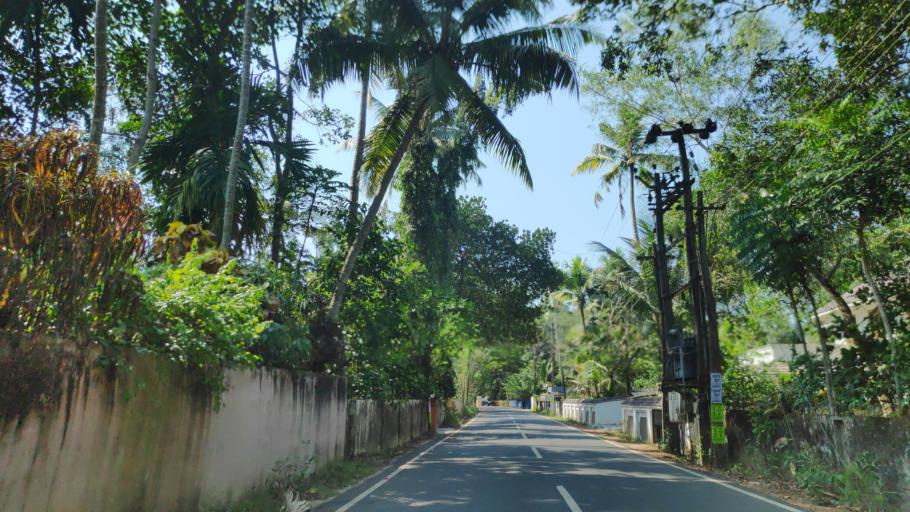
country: IN
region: Kerala
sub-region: Alappuzha
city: Shertallai
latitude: 9.6568
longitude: 76.3348
